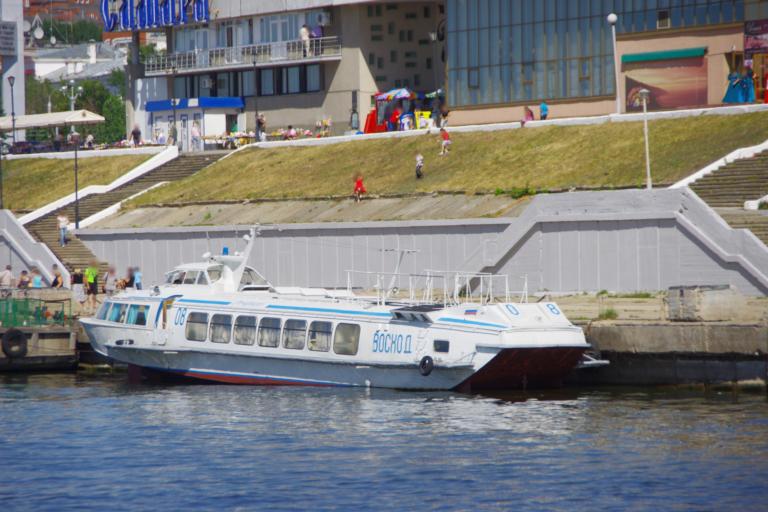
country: RU
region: Samara
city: Rozhdestveno
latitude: 53.1867
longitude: 50.0761
